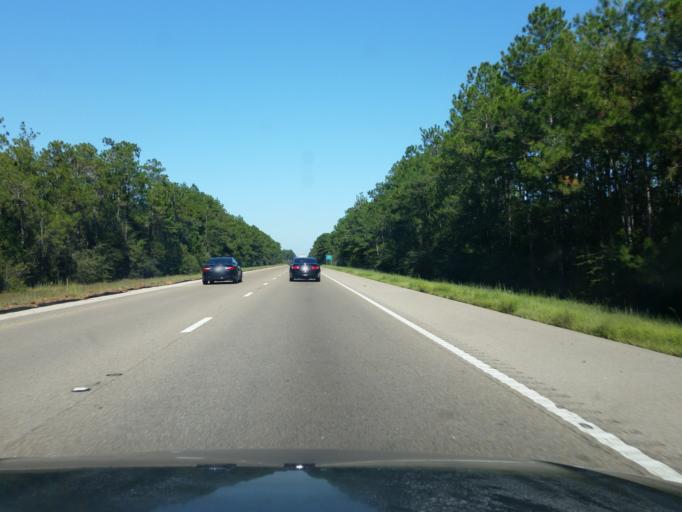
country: US
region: Mississippi
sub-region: Hancock County
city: Kiln
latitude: 30.3356
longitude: -89.5050
